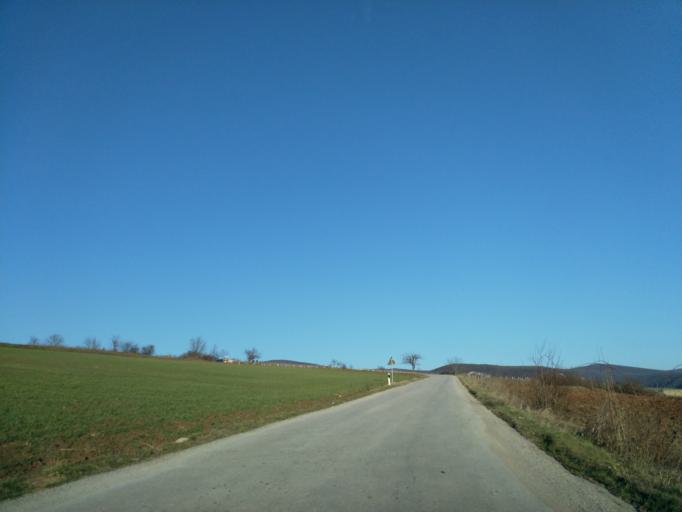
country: RS
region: Central Serbia
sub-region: Pomoravski Okrug
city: Paracin
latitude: 43.9244
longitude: 21.5093
